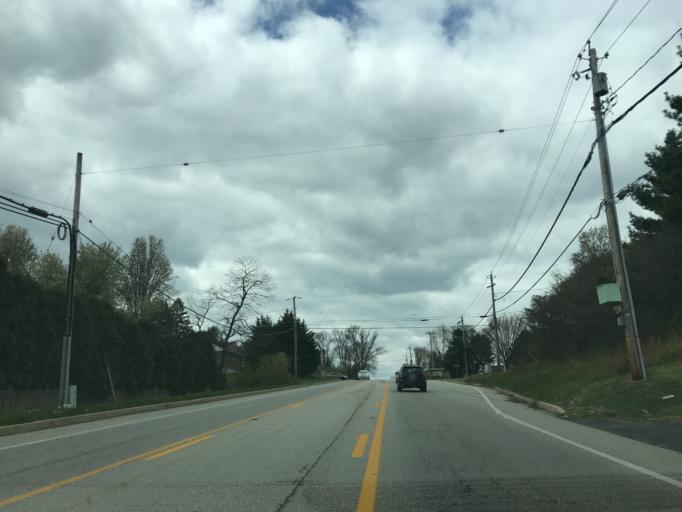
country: US
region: Maryland
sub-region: Harford County
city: South Bel Air
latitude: 39.5387
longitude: -76.3043
